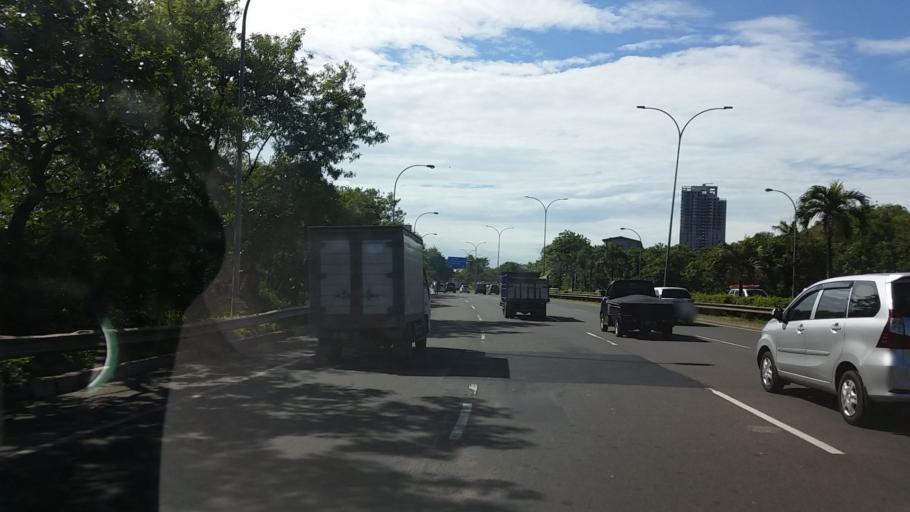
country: ID
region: Banten
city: South Tangerang
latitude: -6.2666
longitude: 106.7679
